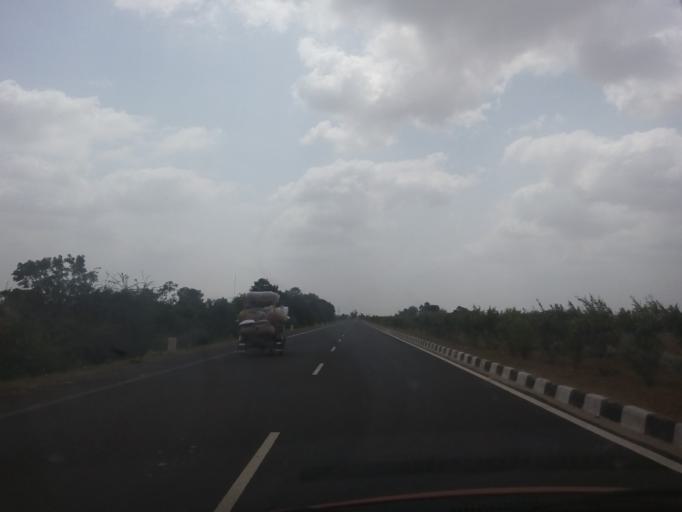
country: IN
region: Gujarat
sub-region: Surendranagar
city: Dhrangadhra
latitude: 23.0005
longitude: 71.5125
